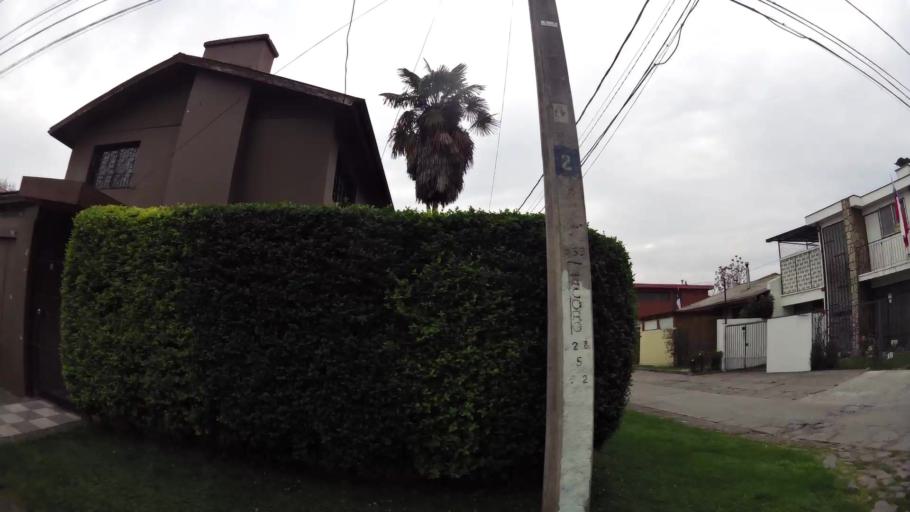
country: CL
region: Santiago Metropolitan
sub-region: Provincia de Santiago
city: Villa Presidente Frei, Nunoa, Santiago, Chile
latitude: -33.4639
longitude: -70.5904
